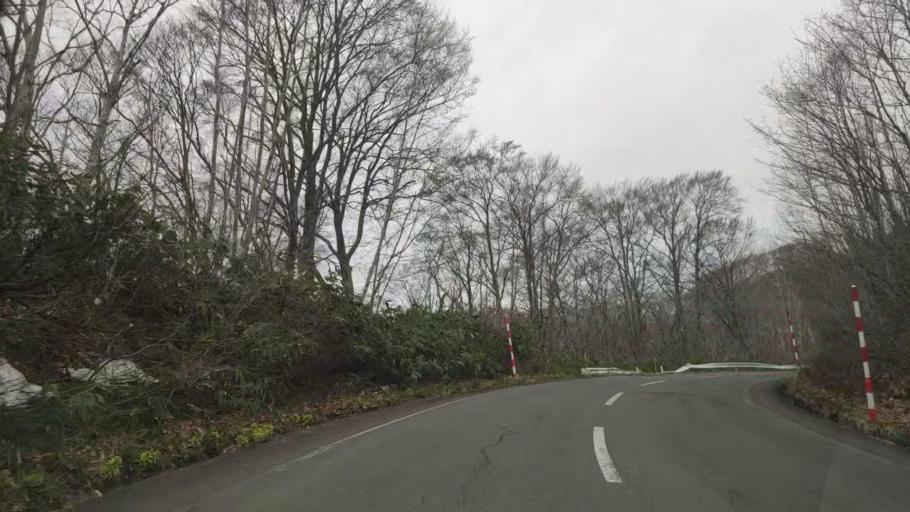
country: JP
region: Akita
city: Hanawa
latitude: 40.4179
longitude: 140.8381
